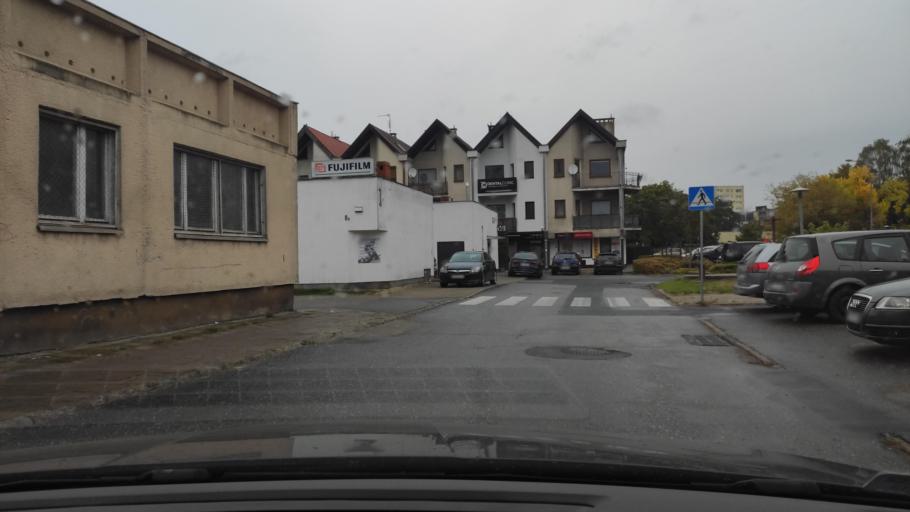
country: PL
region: Greater Poland Voivodeship
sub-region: Powiat poznanski
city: Swarzedz
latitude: 52.4143
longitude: 17.0802
